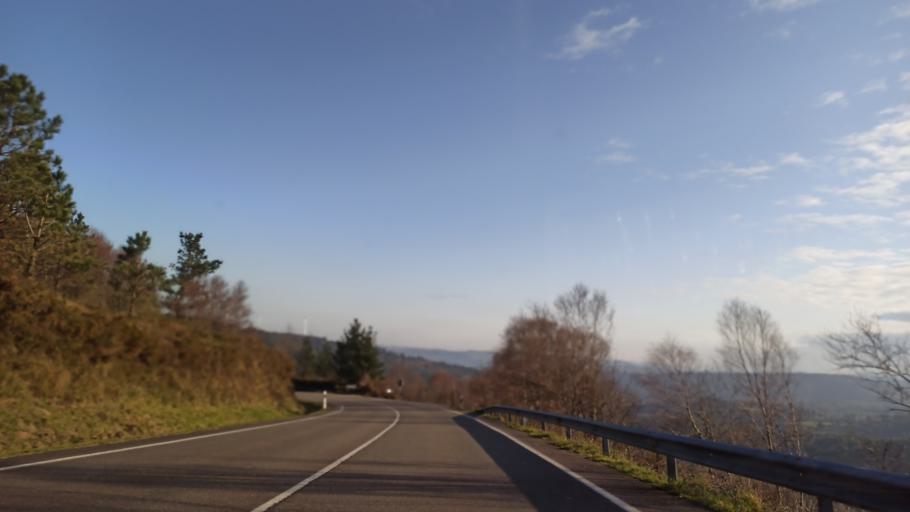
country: ES
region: Galicia
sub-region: Provincia da Coruna
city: As Pontes de Garcia Rodriguez
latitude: 43.5213
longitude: -7.8164
